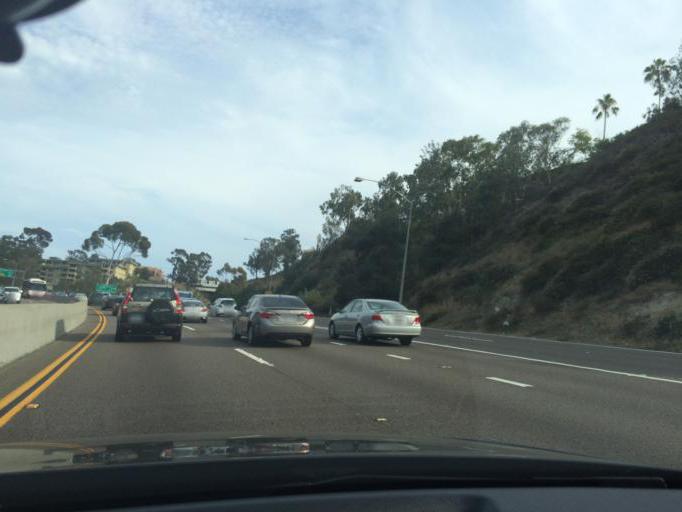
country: US
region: California
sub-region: San Diego County
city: San Diego
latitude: 32.7545
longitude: -117.1586
